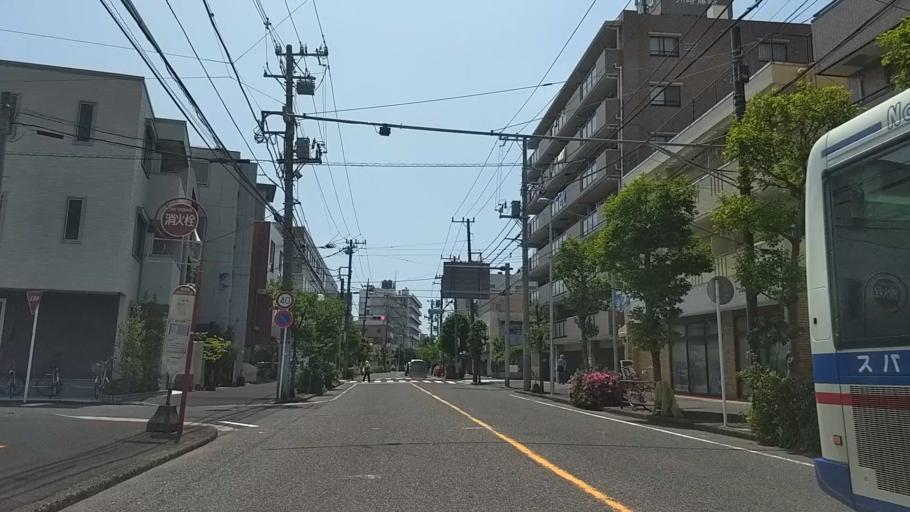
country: JP
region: Kanagawa
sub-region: Kawasaki-shi
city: Kawasaki
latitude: 35.5246
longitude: 139.7225
